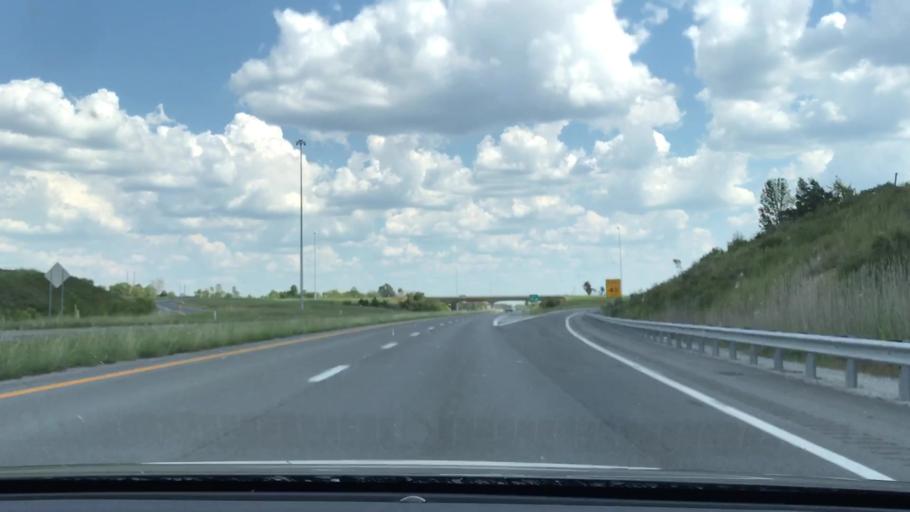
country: US
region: Kentucky
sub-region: Hopkins County
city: Dawson Springs
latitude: 37.1980
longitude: -87.6946
